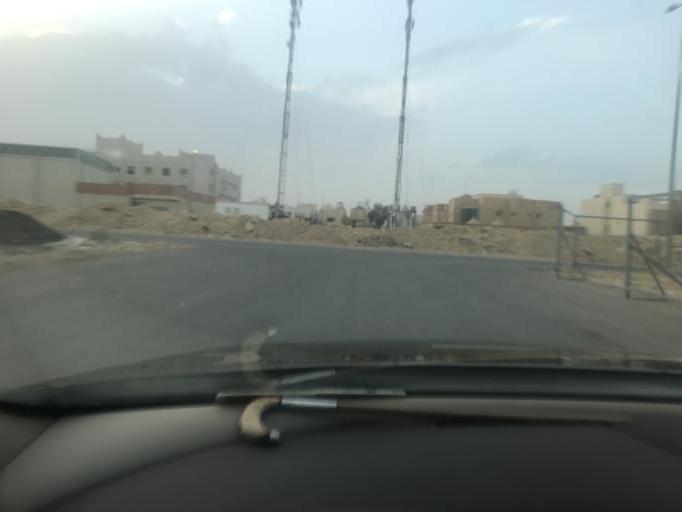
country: SA
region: Ar Riyad
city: Riyadh
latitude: 24.7271
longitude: 46.7481
